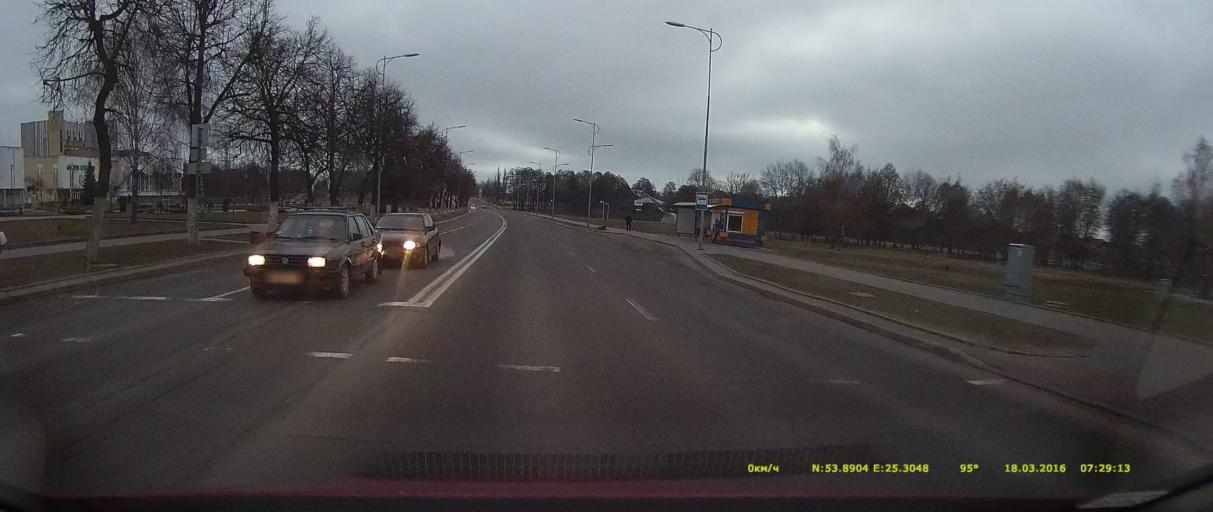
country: BY
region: Grodnenskaya
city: Lida
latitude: 53.8904
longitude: 25.3048
